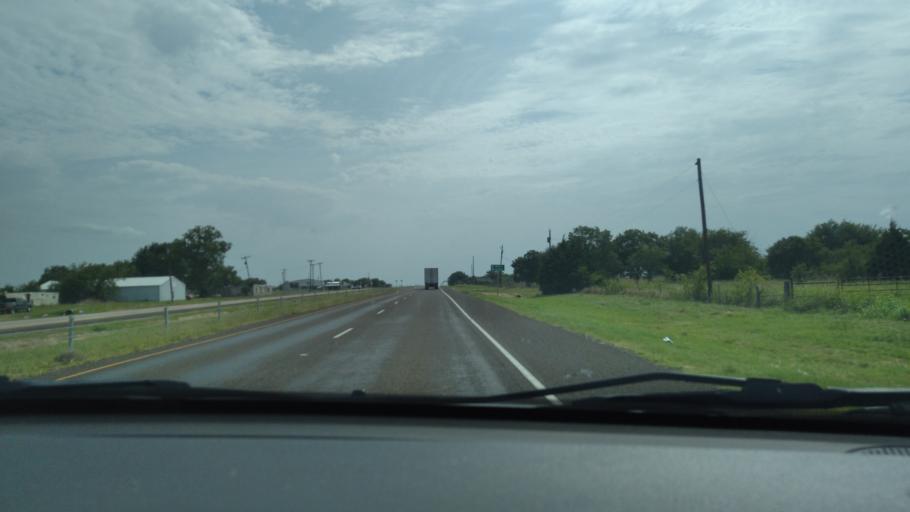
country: US
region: Texas
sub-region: Navarro County
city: Corsicana
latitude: 32.0383
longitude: -96.5473
